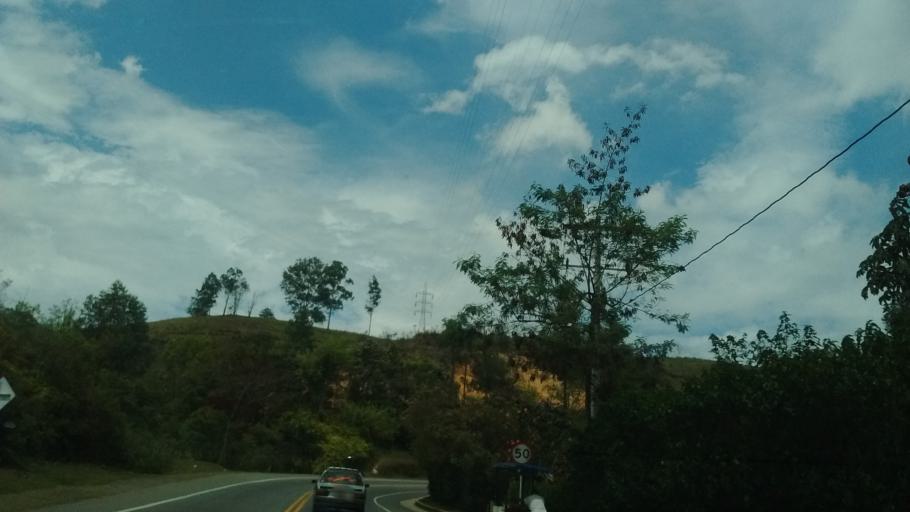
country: CO
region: Cauca
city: Popayan
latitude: 2.4241
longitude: -76.6278
